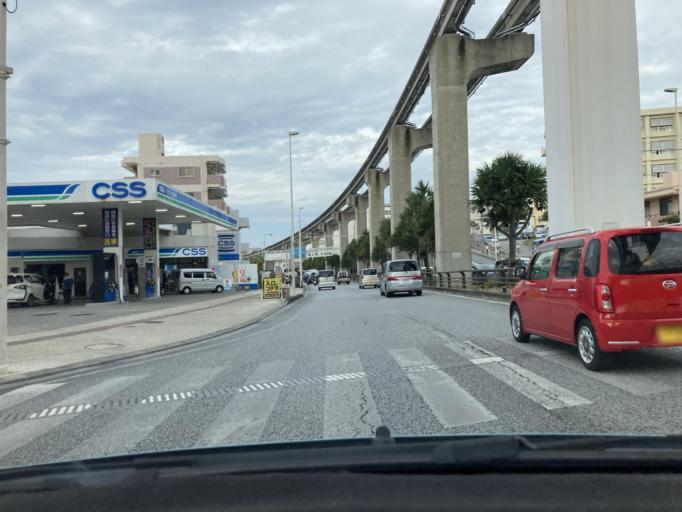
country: JP
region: Okinawa
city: Naha-shi
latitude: 26.2278
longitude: 127.7015
